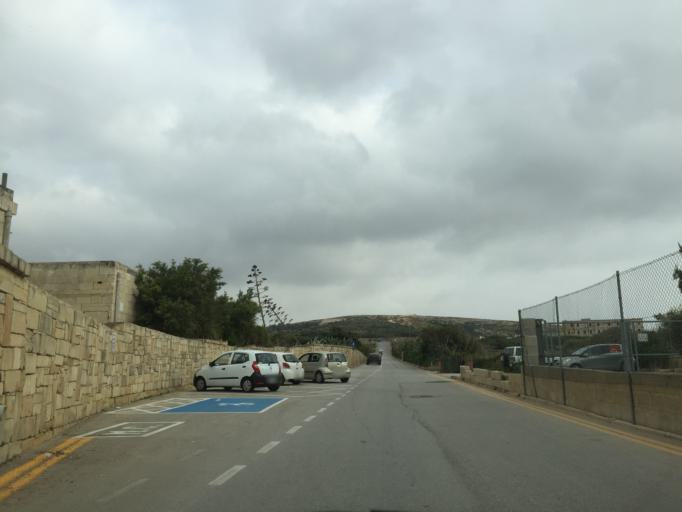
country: MT
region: L-Imgarr
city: Imgarr
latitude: 35.9338
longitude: 14.3463
